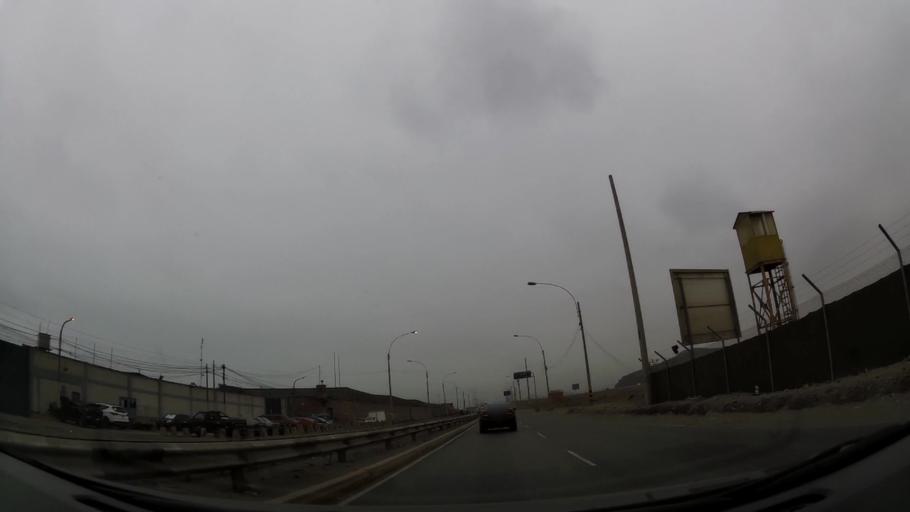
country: PE
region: Callao
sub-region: Callao
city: Callao
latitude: -12.0022
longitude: -77.1268
